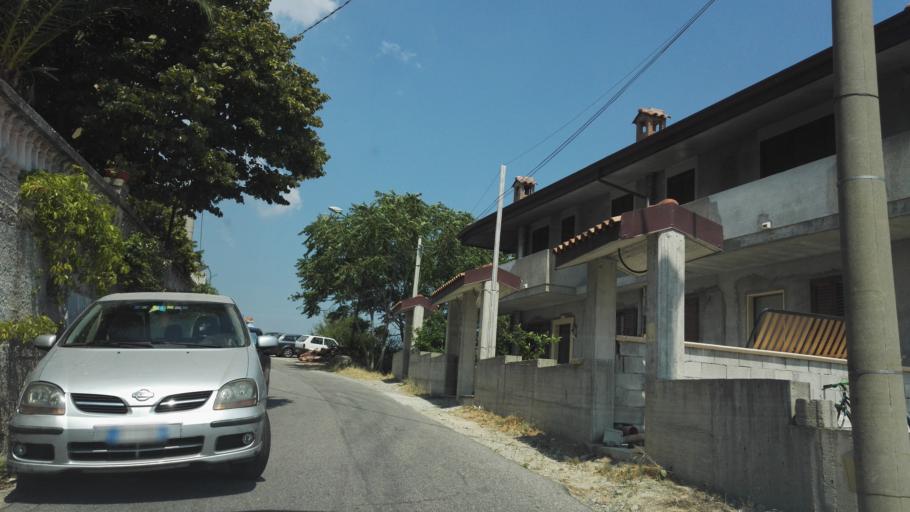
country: IT
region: Calabria
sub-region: Provincia di Reggio Calabria
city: Stilo
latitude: 38.4759
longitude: 16.4719
